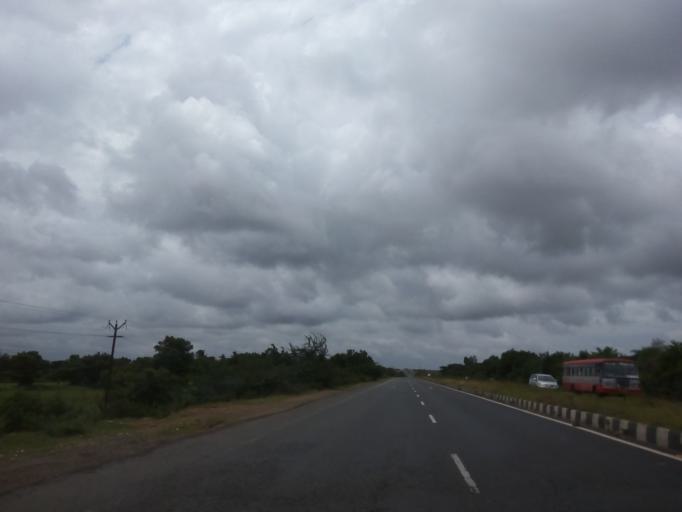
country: IN
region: Karnataka
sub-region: Haveri
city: Ranibennur
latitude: 14.6620
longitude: 75.5634
